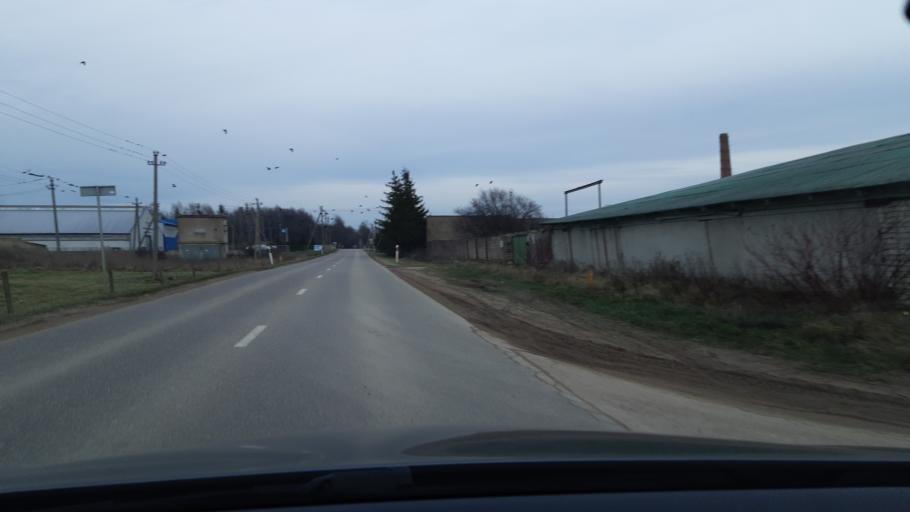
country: LT
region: Kauno apskritis
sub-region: Kaunas
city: Sargenai
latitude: 54.9546
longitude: 23.8580
